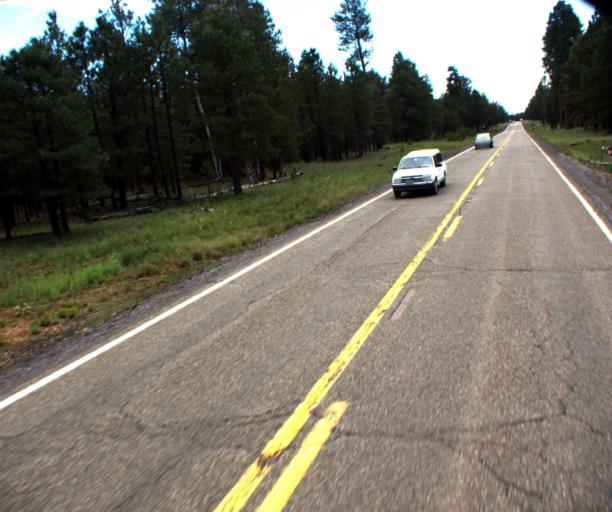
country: US
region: Arizona
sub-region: Coconino County
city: Parks
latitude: 35.3741
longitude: -111.7900
